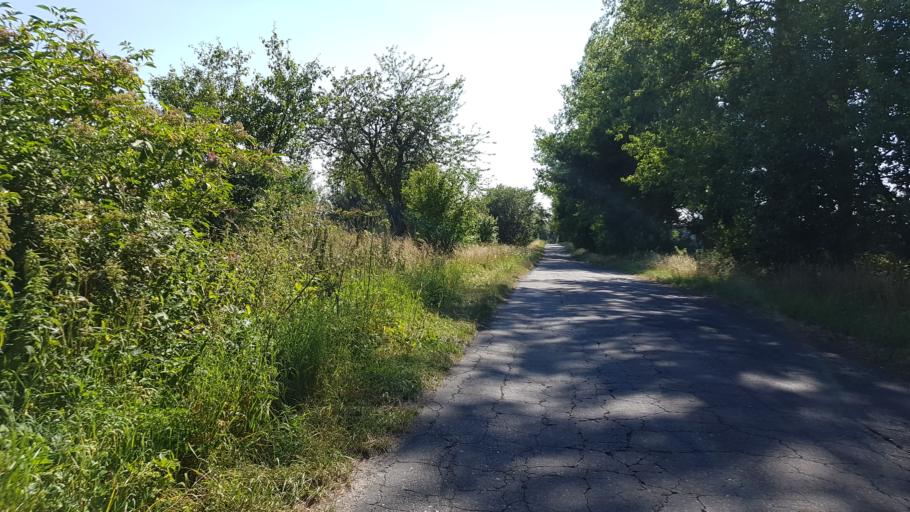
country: PL
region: West Pomeranian Voivodeship
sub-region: Powiat gryfinski
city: Gryfino
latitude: 53.1676
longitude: 14.5333
